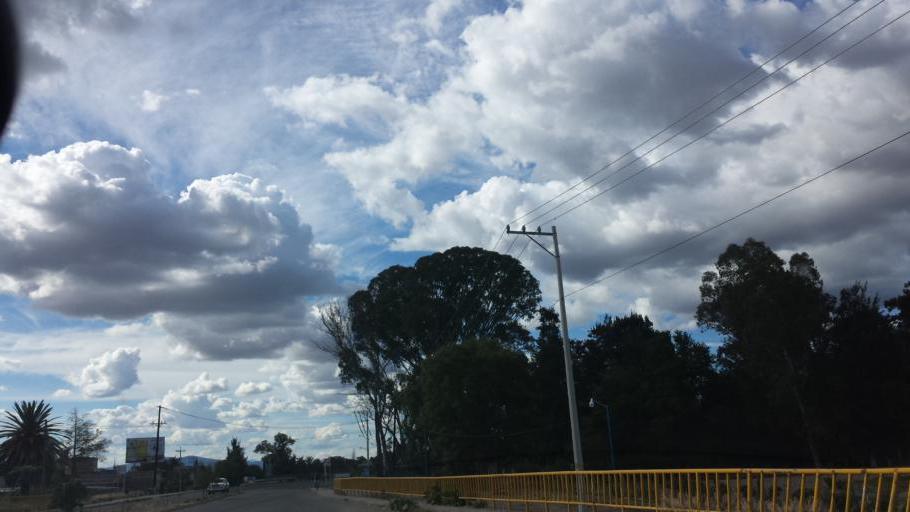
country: MX
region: Oaxaca
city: Tlacolula de Matamoros
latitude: 16.9511
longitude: -96.4658
